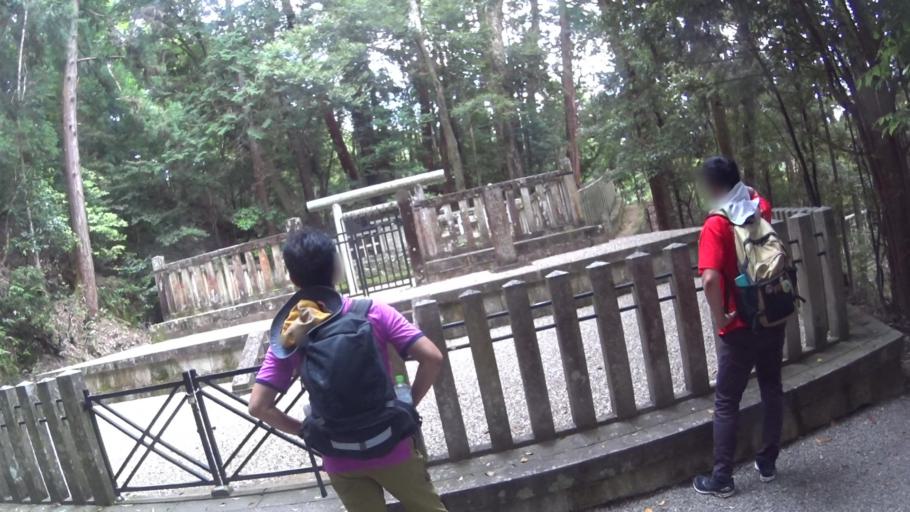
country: JP
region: Nara
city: Yoshino-cho
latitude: 34.3647
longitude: 135.8687
